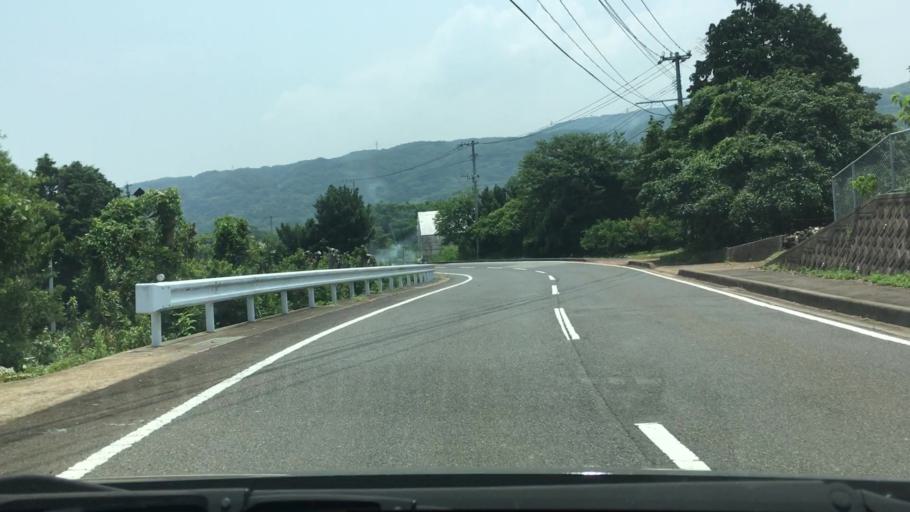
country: JP
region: Nagasaki
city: Sasebo
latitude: 33.0686
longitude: 129.6810
